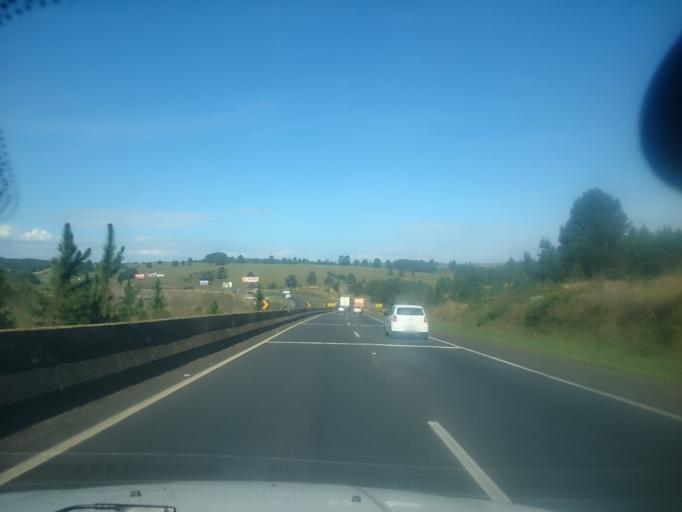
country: BR
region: Parana
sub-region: Campo Largo
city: Campo Largo
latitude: -25.4376
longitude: -49.7506
